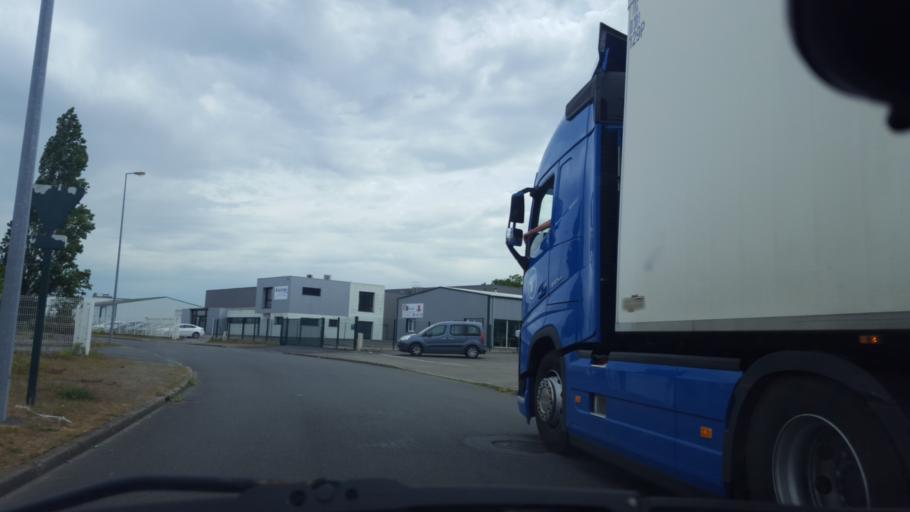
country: FR
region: Pays de la Loire
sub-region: Departement de la Loire-Atlantique
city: Machecoul
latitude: 46.9821
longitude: -1.8079
